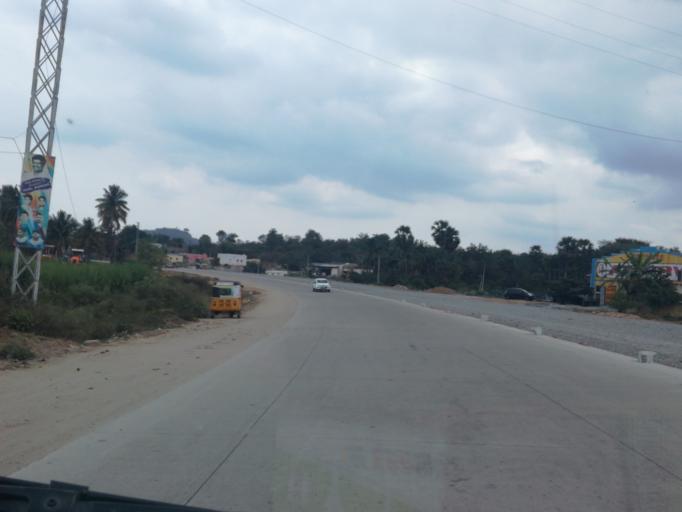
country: IN
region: Andhra Pradesh
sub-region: Chittoor
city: Ramapuram
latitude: 13.0965
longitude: 79.1264
